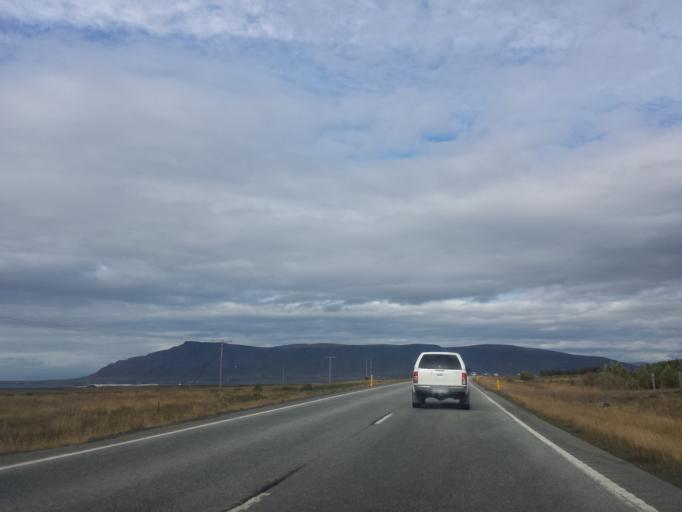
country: IS
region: Capital Region
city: Reykjavik
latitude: 64.2554
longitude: -21.8309
